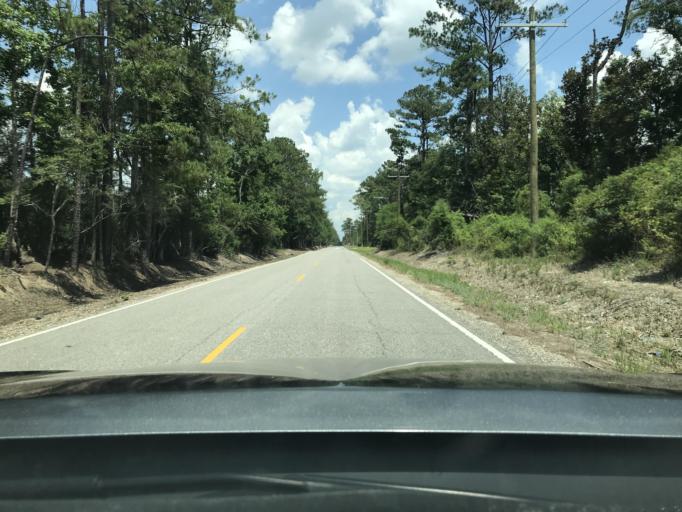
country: US
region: Louisiana
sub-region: Calcasieu Parish
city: Moss Bluff
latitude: 30.3300
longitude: -93.1553
